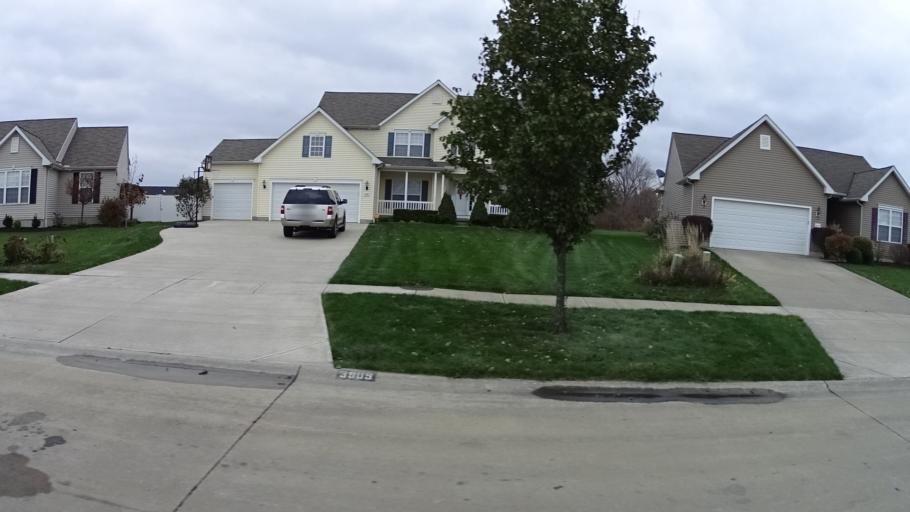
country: US
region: Ohio
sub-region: Lorain County
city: Amherst
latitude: 41.4299
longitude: -82.2180
